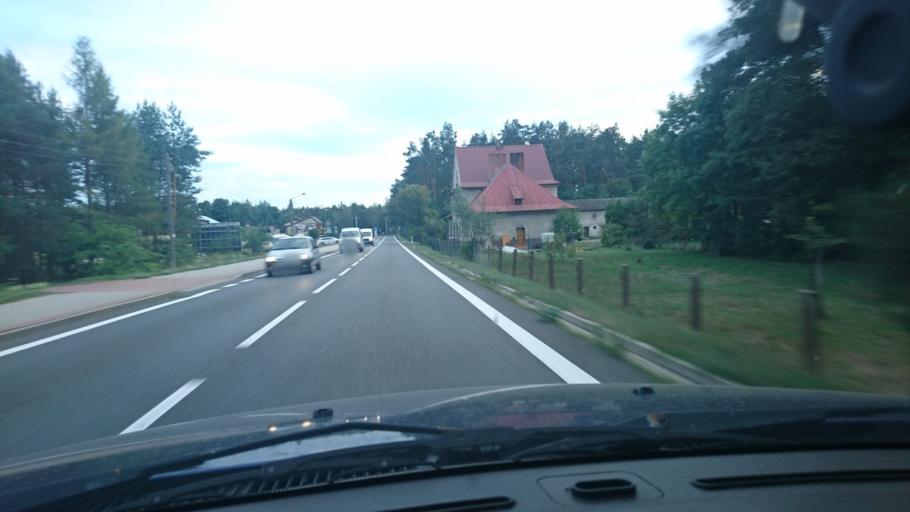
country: PL
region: Silesian Voivodeship
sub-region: Powiat tarnogorski
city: Tworog
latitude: 50.5938
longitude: 18.7014
